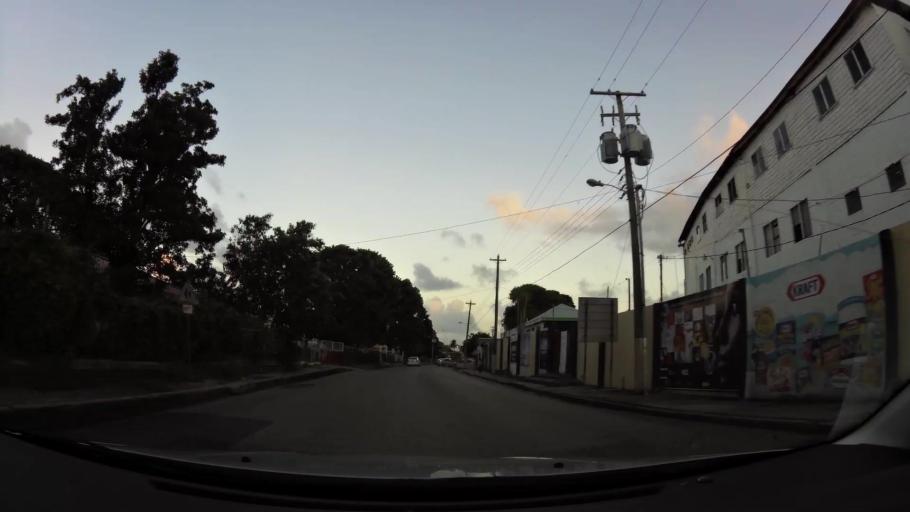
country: AG
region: Saint John
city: Saint John's
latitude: 17.1233
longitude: -61.8392
